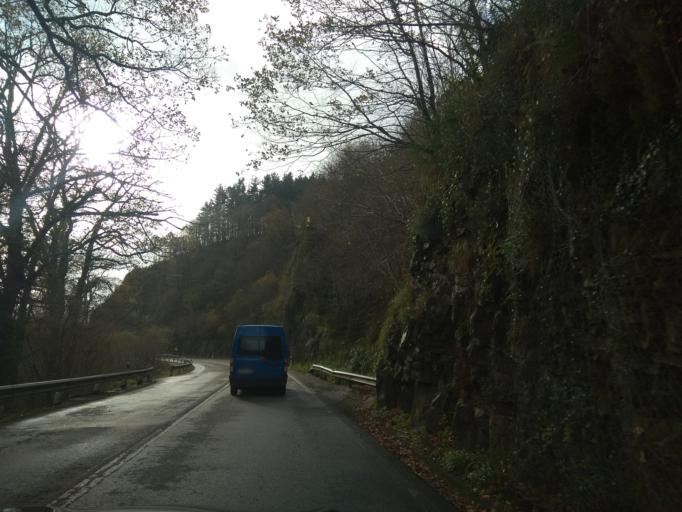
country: ES
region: Cantabria
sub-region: Provincia de Cantabria
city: San Pedro del Romeral
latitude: 43.1430
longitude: -3.8998
